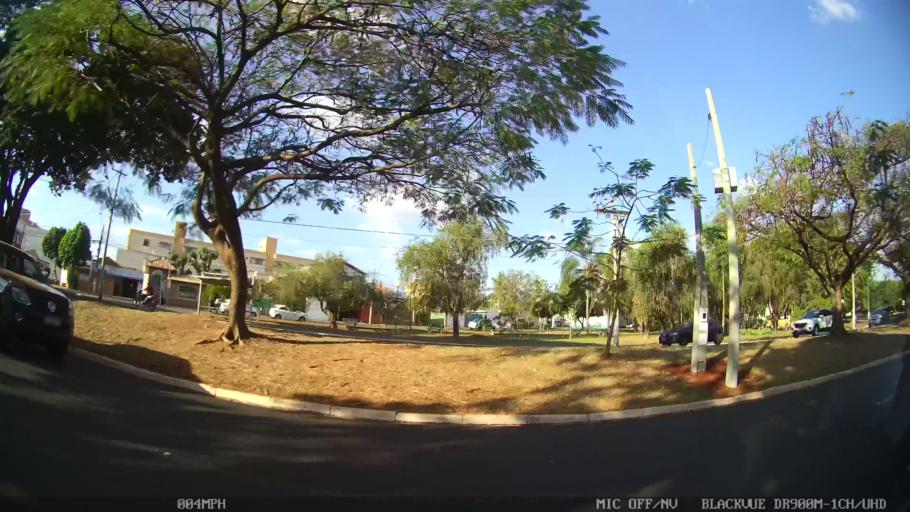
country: BR
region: Sao Paulo
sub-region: Ribeirao Preto
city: Ribeirao Preto
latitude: -21.1852
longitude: -47.7860
